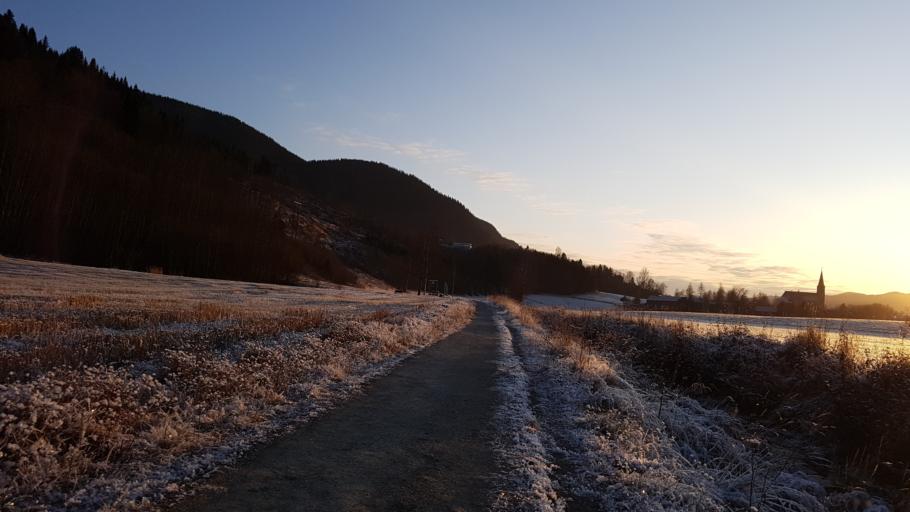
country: NO
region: Sor-Trondelag
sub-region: Melhus
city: Melhus
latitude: 63.2802
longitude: 10.3006
